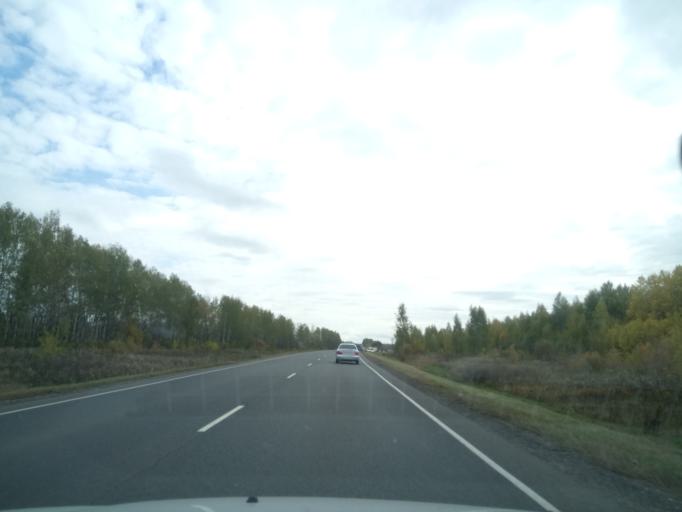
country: RU
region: Nizjnij Novgorod
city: Lukoyanov
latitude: 55.0602
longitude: 44.3618
